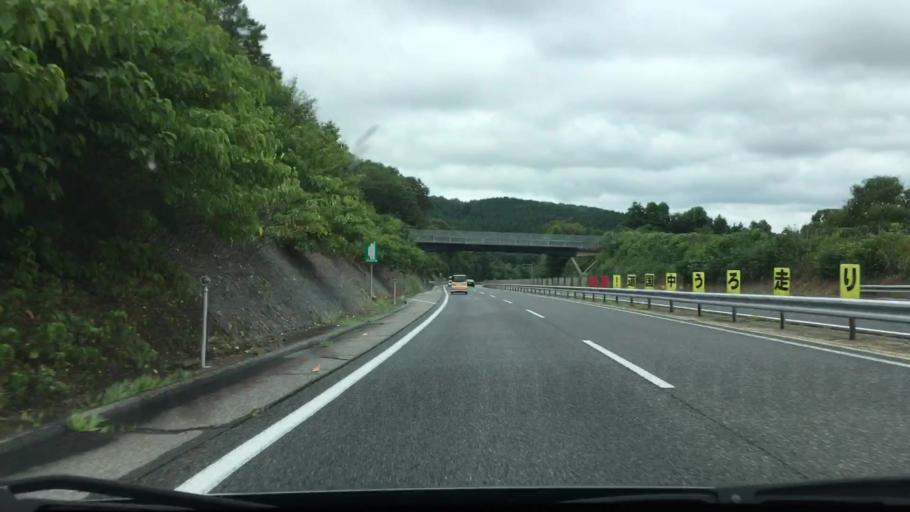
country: JP
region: Hiroshima
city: Miyoshi
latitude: 34.7765
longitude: 132.8382
